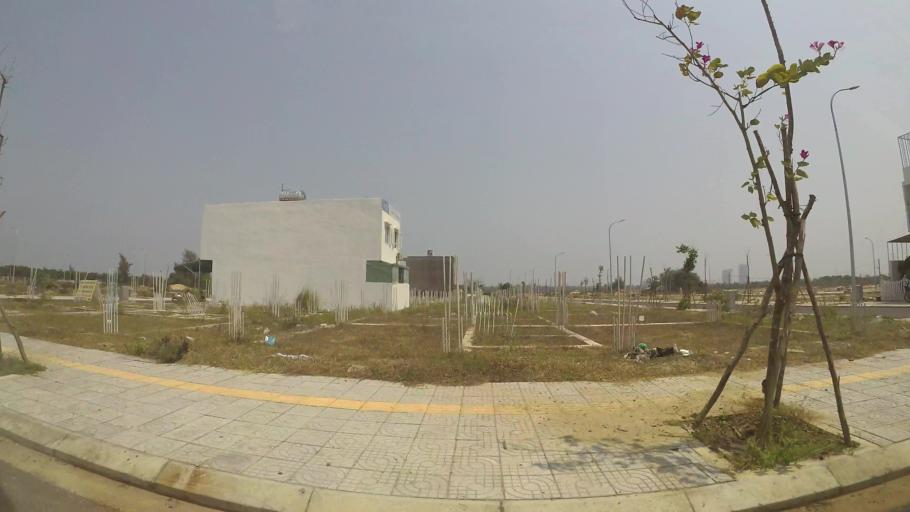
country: VN
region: Da Nang
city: Ngu Hanh Son
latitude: 15.9760
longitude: 108.2614
